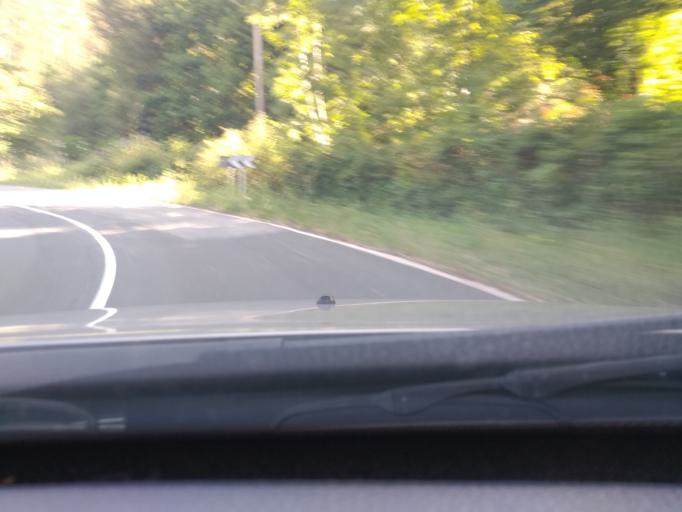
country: ES
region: Basque Country
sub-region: Bizkaia
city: Bakio
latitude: 43.4361
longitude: -2.7808
